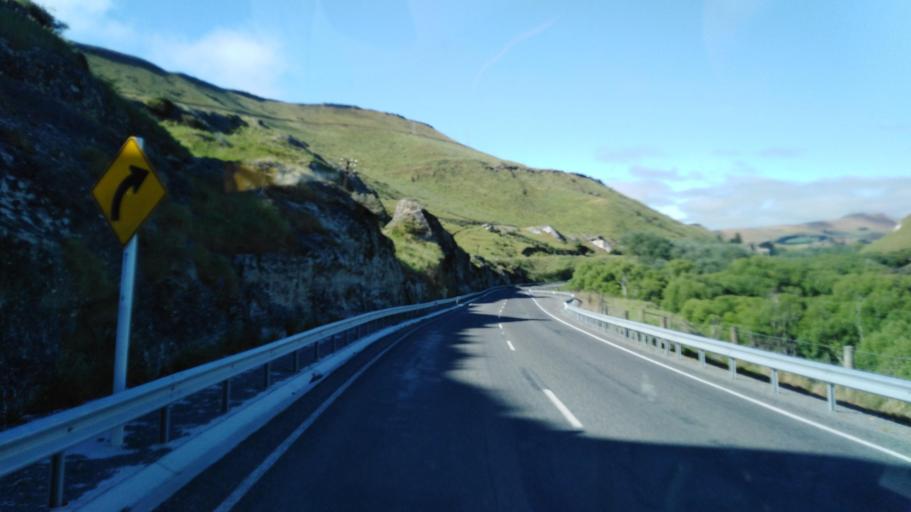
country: NZ
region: Canterbury
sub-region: Hurunui District
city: Amberley
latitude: -42.9946
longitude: 172.7201
